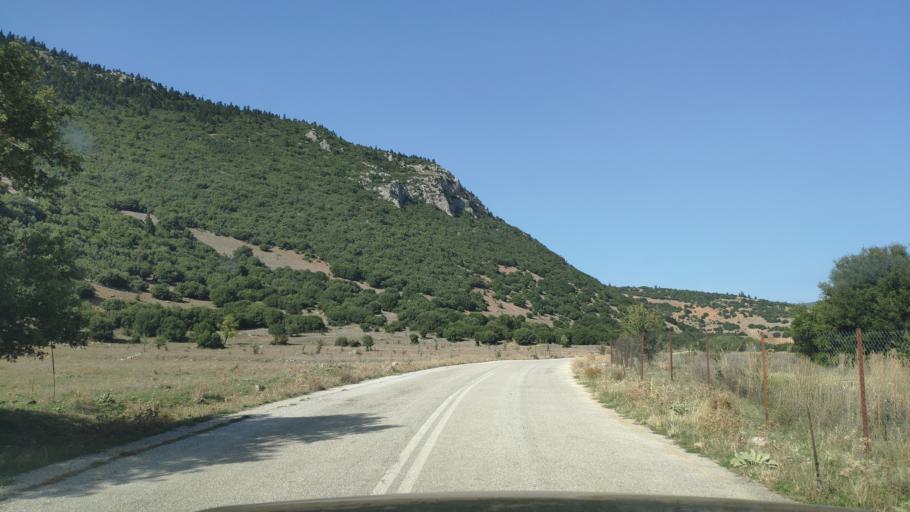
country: GR
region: West Greece
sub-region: Nomos Achaias
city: Aiyira
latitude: 37.9618
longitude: 22.3454
